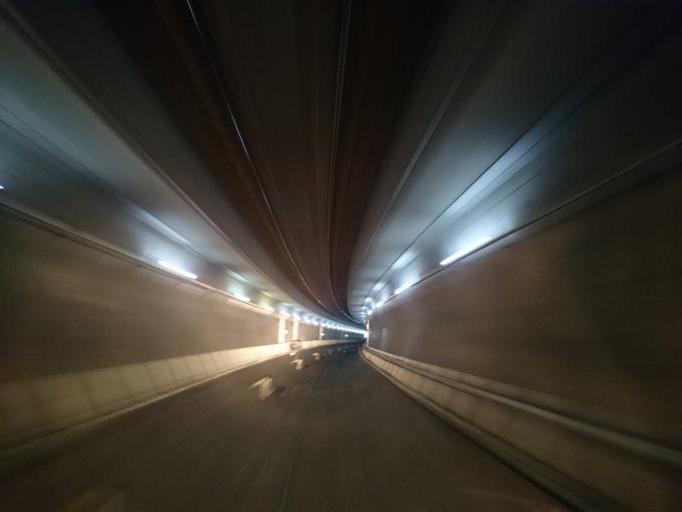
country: SE
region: Skane
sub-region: Malmo
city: Malmoe
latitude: 55.5964
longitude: 12.9984
